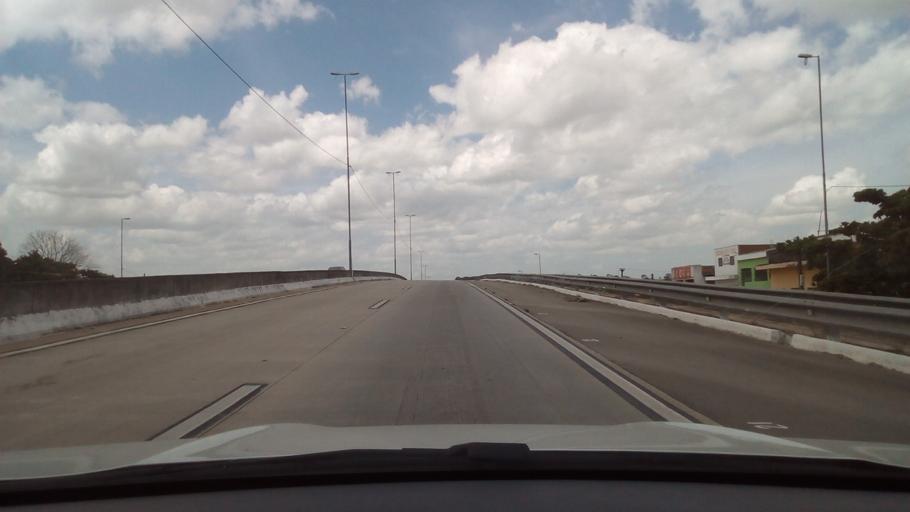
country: BR
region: Paraiba
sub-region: Mamanguape
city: Mamanguape
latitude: -6.8405
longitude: -35.1362
